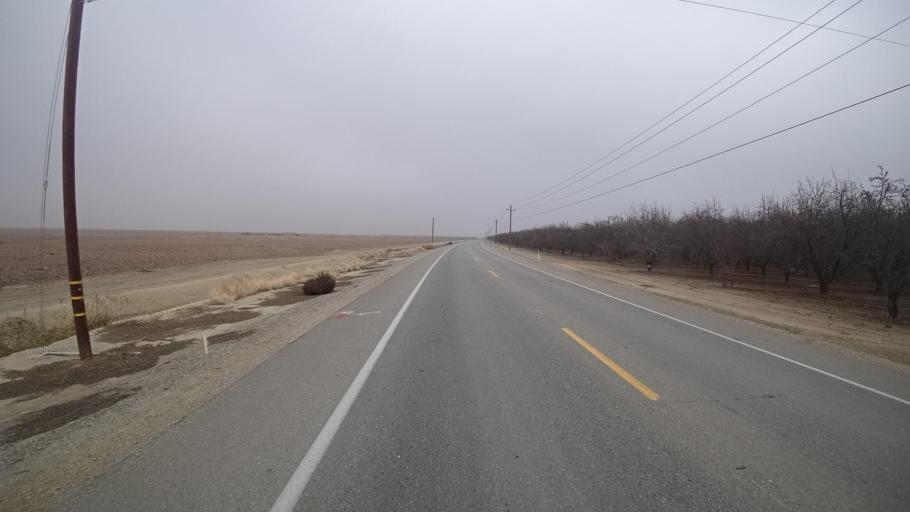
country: US
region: California
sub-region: Kern County
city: Greenfield
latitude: 35.0779
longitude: -119.1251
